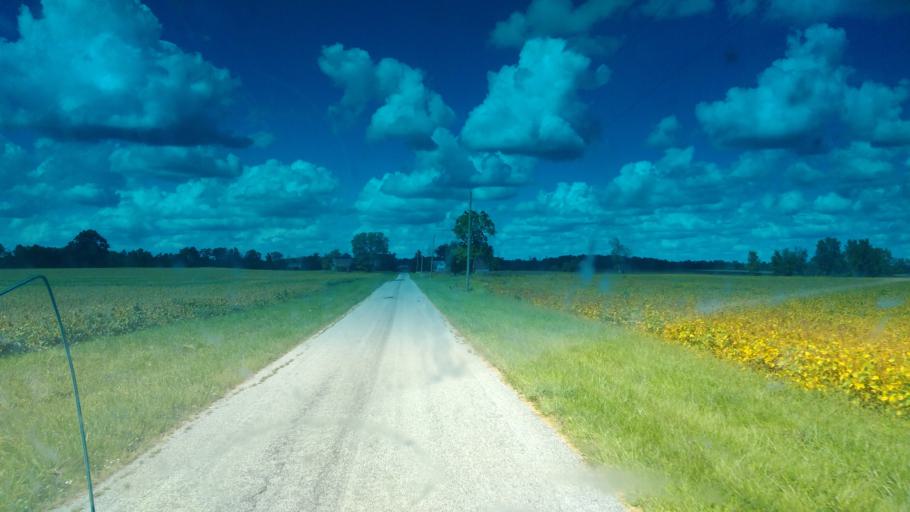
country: US
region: Ohio
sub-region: Hardin County
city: Kenton
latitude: 40.4849
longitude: -83.4992
